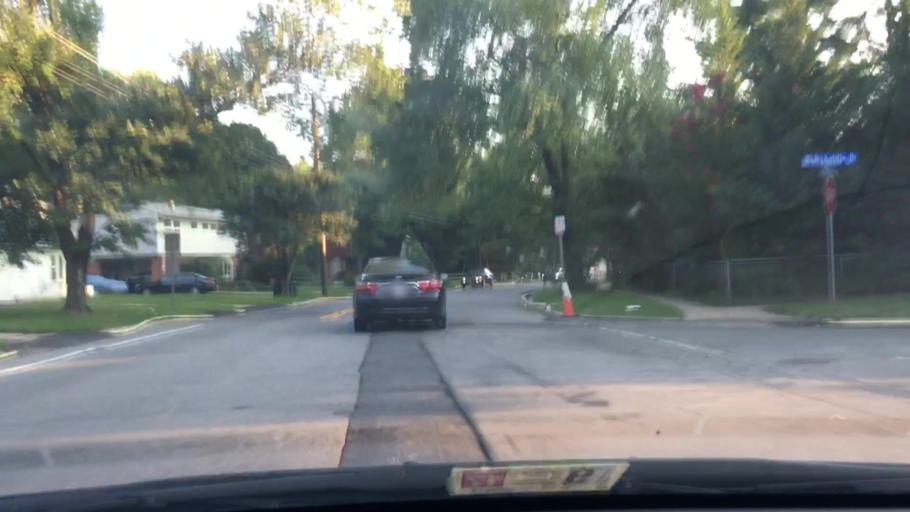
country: US
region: Maryland
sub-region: Montgomery County
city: North Bethesda
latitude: 39.0745
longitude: -77.1114
